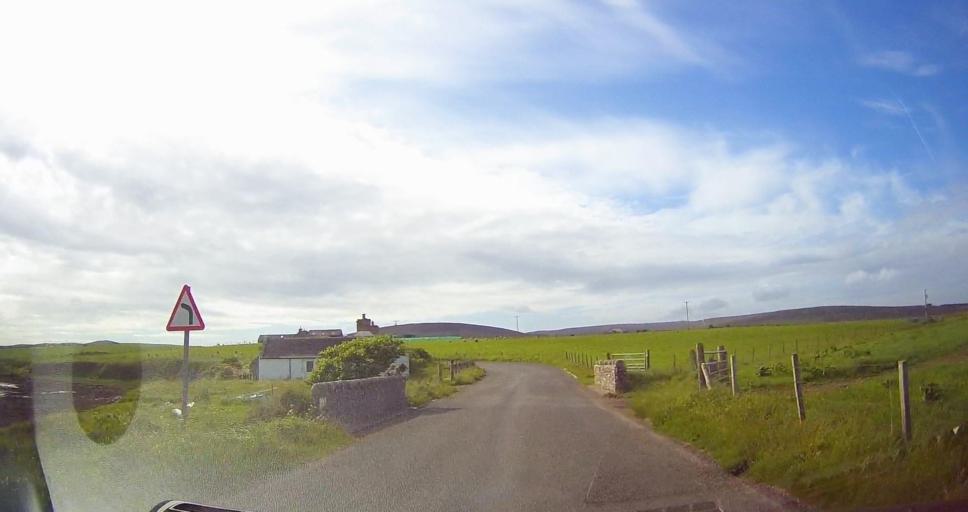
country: GB
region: Scotland
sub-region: Orkney Islands
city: Stromness
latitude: 58.8069
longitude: -3.2089
